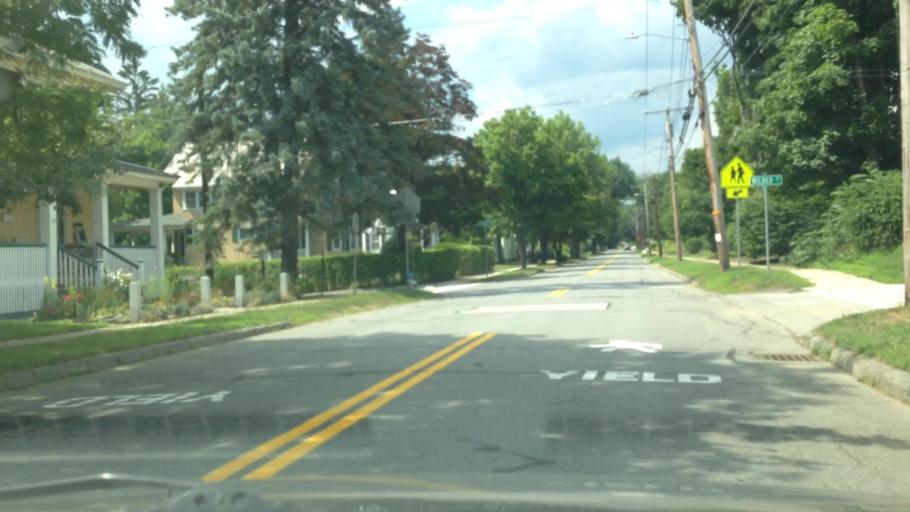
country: US
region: New Hampshire
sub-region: Cheshire County
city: Keene
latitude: 42.9337
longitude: -72.2668
